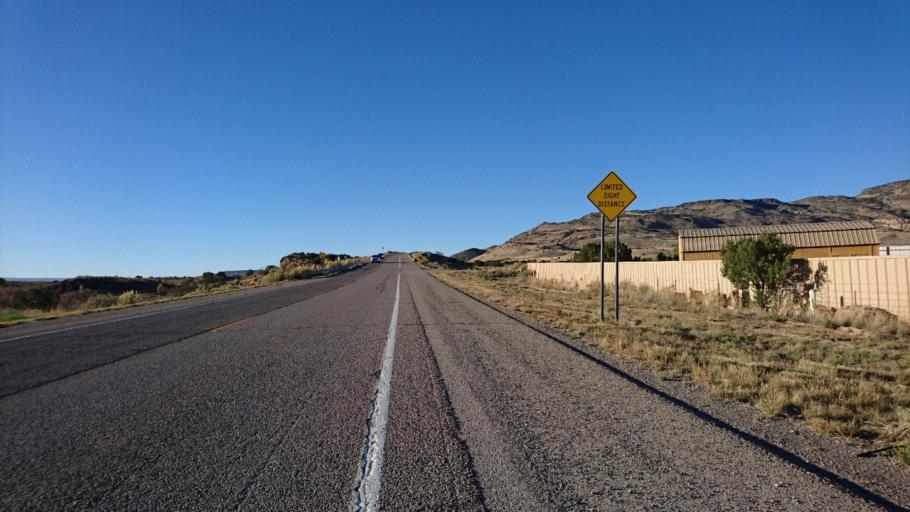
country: US
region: New Mexico
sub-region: Cibola County
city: Grants
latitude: 35.1032
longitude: -107.7779
